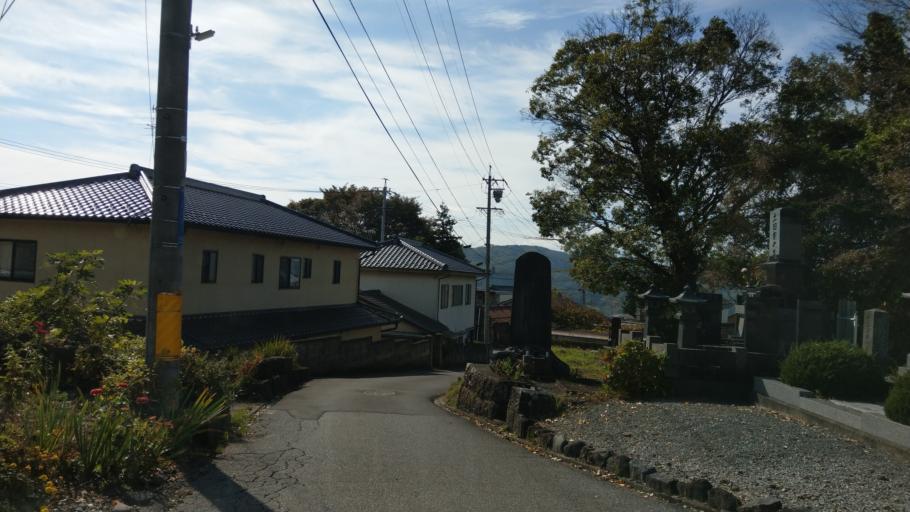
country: JP
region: Nagano
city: Komoro
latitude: 36.3240
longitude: 138.4342
